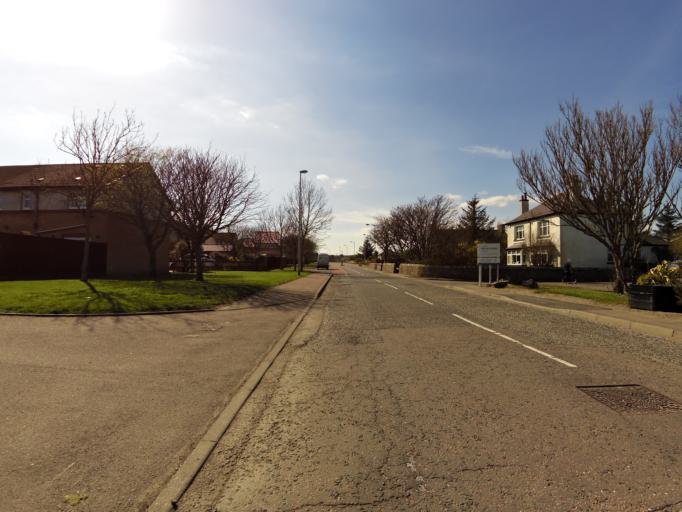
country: GB
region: Scotland
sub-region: Aberdeen City
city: Aberdeen
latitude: 57.0986
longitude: -2.0825
